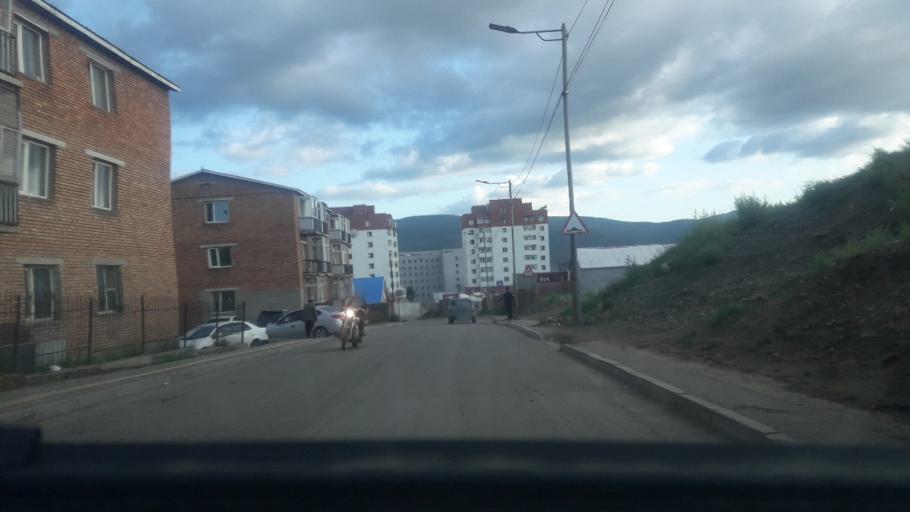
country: MN
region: Ulaanbaatar
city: Ulaanbaatar
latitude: 47.9191
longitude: 106.9954
